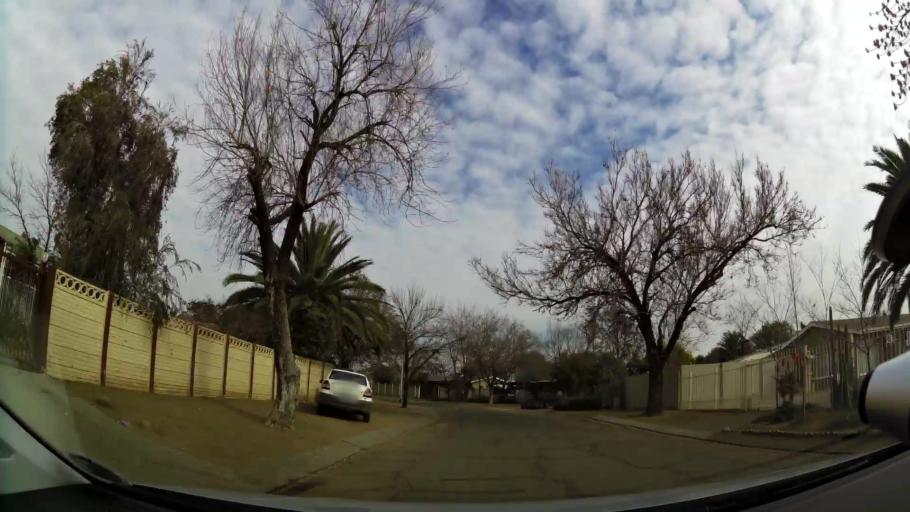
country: ZA
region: Orange Free State
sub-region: Mangaung Metropolitan Municipality
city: Bloemfontein
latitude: -29.1324
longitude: 26.1942
